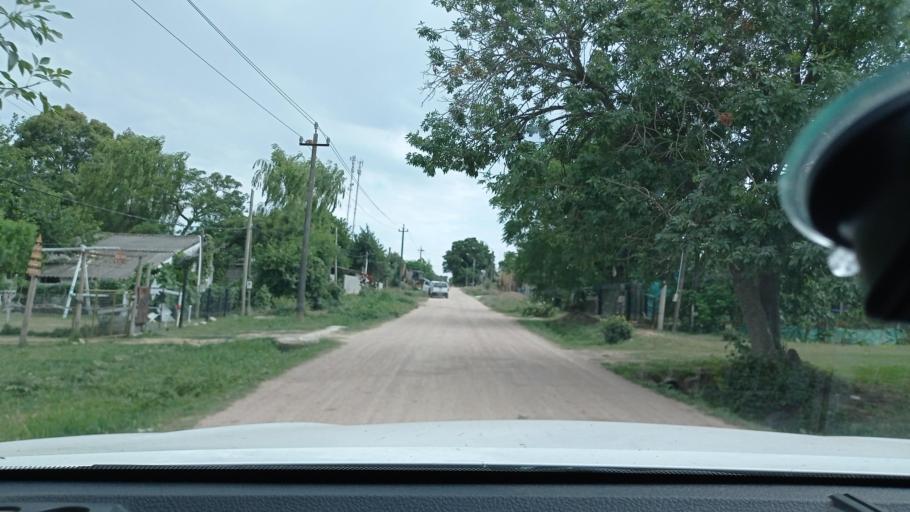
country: UY
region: Canelones
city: Pando
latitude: -34.7096
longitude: -55.9688
